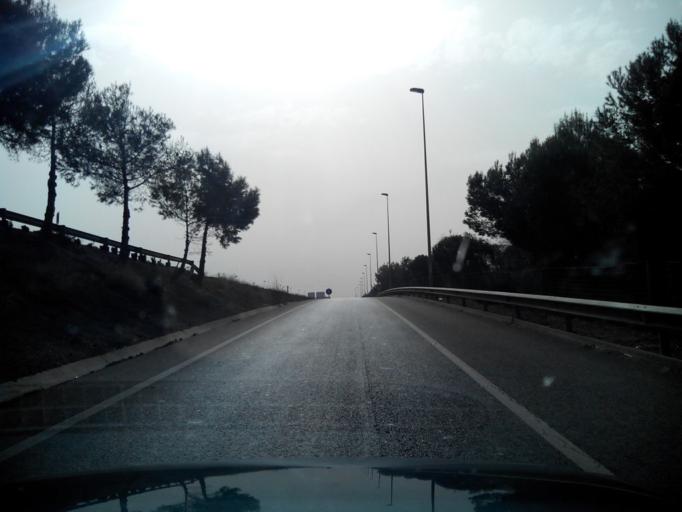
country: ES
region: Catalonia
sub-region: Provincia de Tarragona
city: Reus
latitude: 41.1390
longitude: 1.0987
